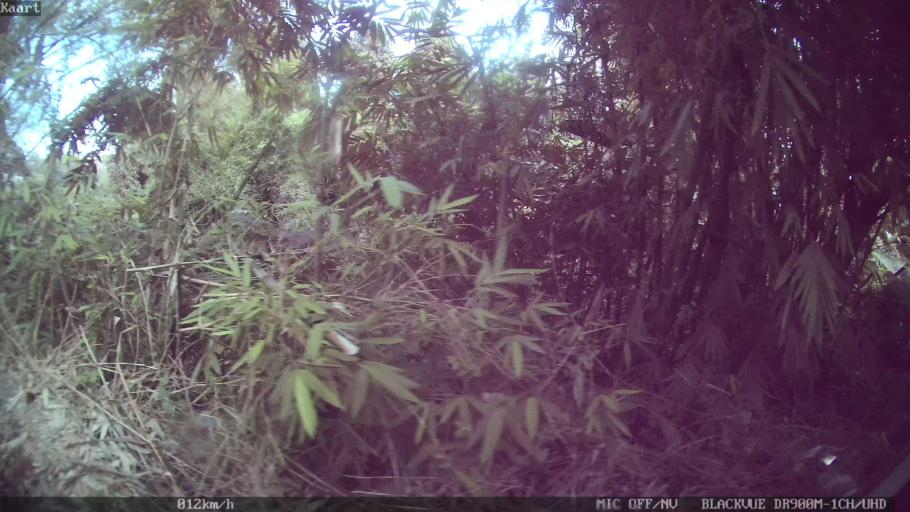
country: ID
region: Bali
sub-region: Kabupaten Gianyar
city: Ubud
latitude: -8.5095
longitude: 115.2782
